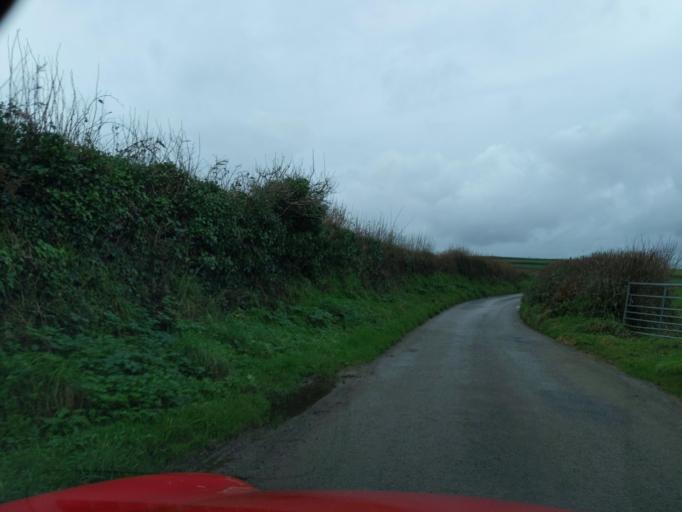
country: GB
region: England
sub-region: Cornwall
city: Duloe
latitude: 50.3467
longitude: -4.5349
